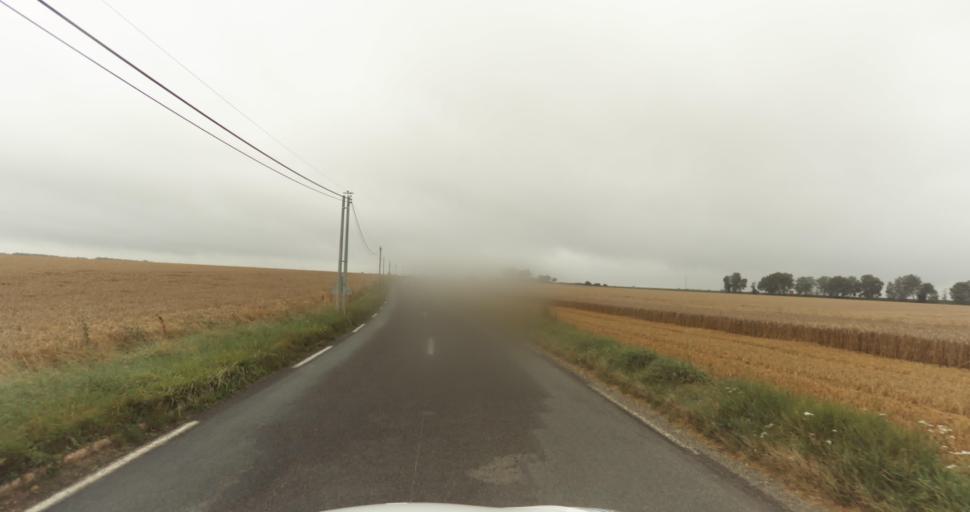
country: FR
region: Haute-Normandie
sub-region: Departement de l'Eure
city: Normanville
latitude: 49.0899
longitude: 1.1942
